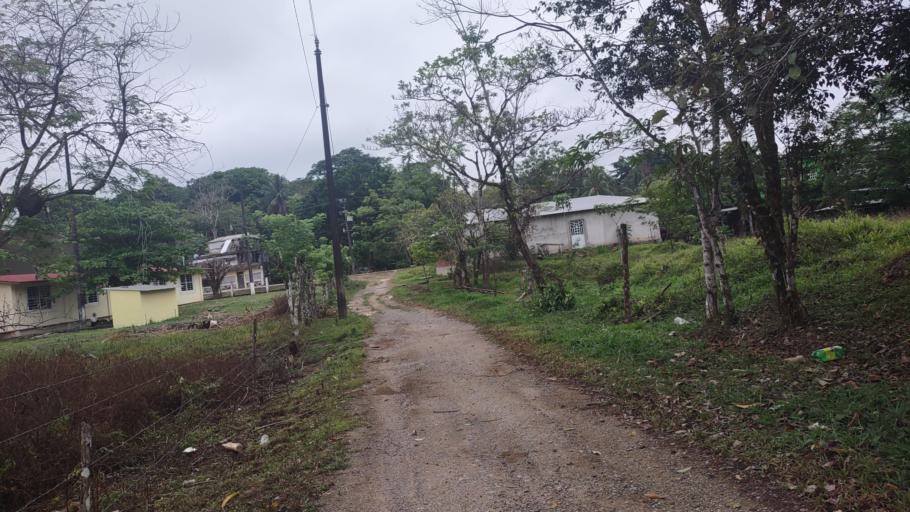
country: MX
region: Veracruz
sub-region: Uxpanapa
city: Poblado 10
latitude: 17.4749
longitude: -94.1217
